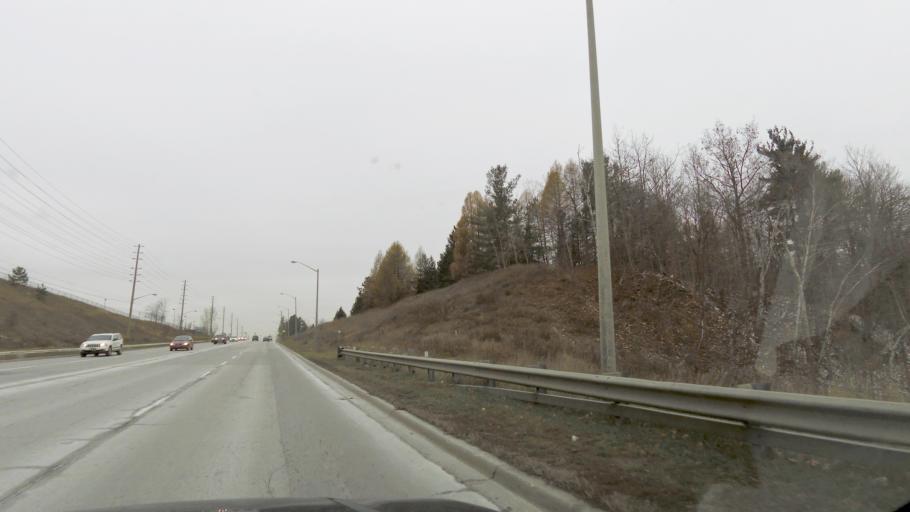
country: CA
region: Ontario
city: Vaughan
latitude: 43.8191
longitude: -79.5913
